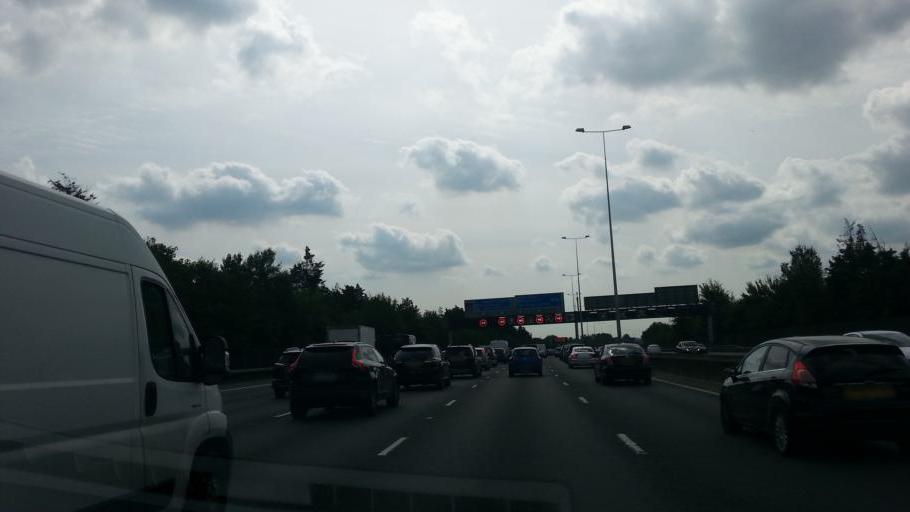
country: GB
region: England
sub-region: Surrey
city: Egham
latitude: 51.4219
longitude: -0.5397
